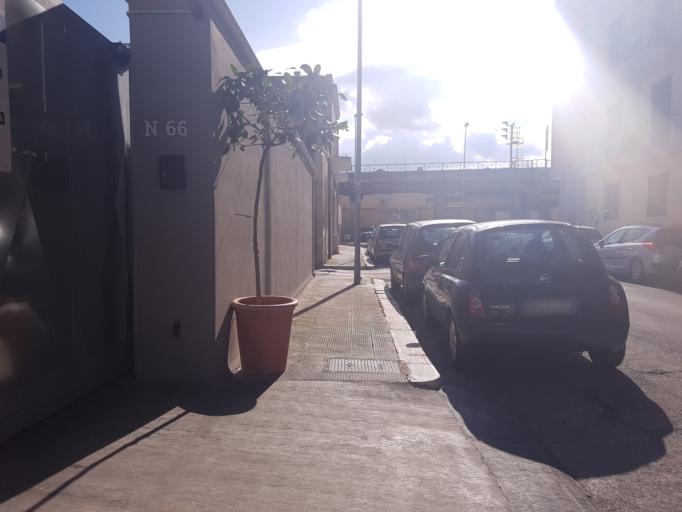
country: IT
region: Apulia
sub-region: Provincia di Bari
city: Bari
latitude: 41.1186
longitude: 16.8532
